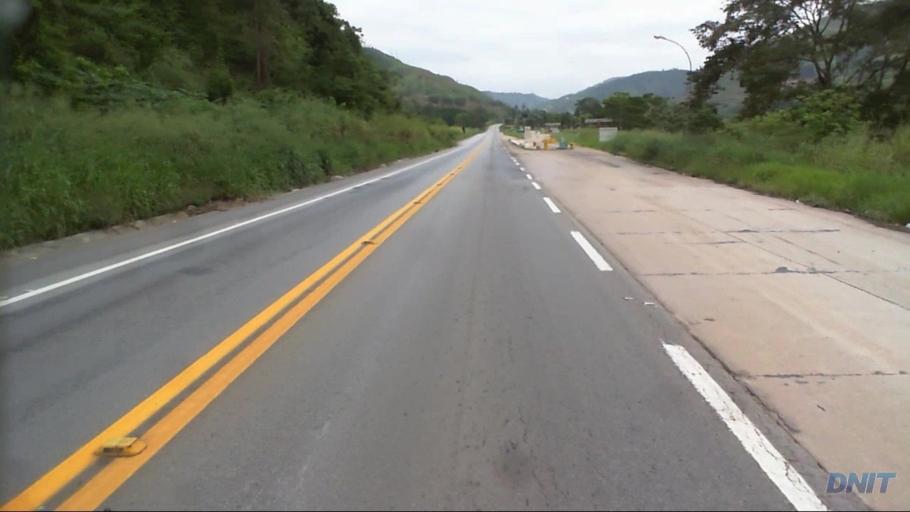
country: BR
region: Minas Gerais
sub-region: Timoteo
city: Timoteo
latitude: -19.5938
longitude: -42.7408
